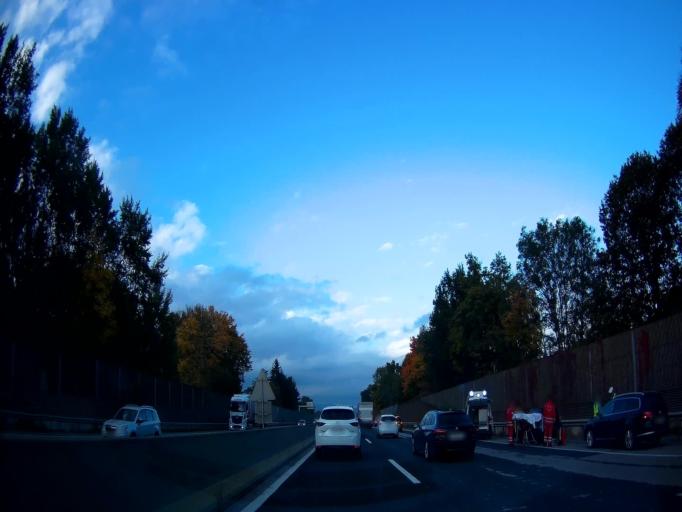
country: AT
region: Styria
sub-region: Politischer Bezirk Graz-Umgebung
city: Unterpremstatten
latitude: 46.9809
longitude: 15.3945
